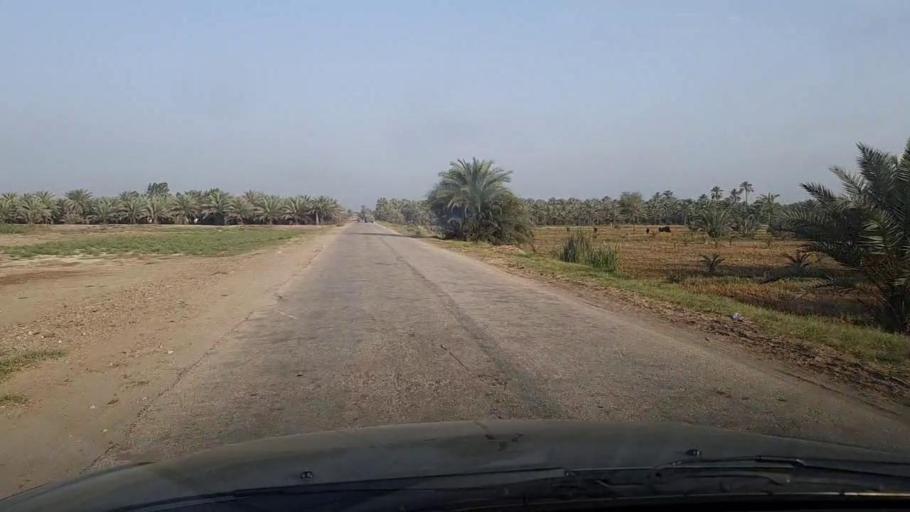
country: PK
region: Sindh
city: Khairpur
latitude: 27.5407
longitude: 68.7081
